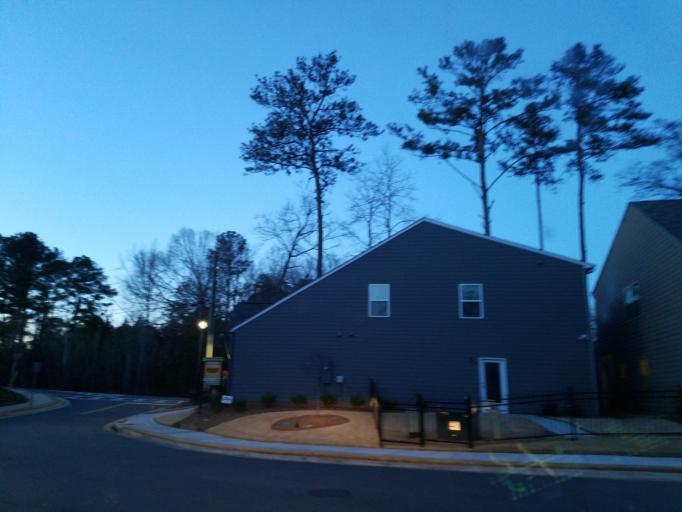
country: US
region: Georgia
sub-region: Cherokee County
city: Holly Springs
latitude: 34.1689
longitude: -84.4121
